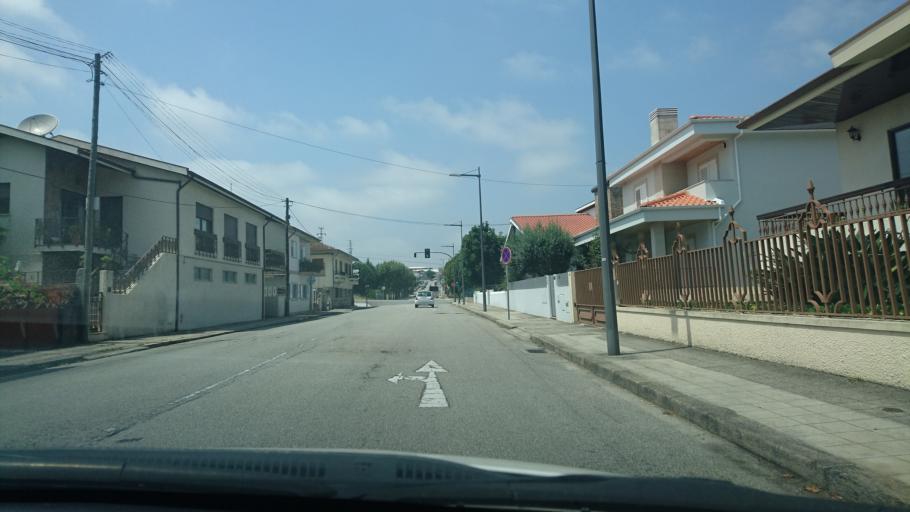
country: PT
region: Porto
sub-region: Valongo
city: Valongo
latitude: 41.1904
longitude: -8.5035
